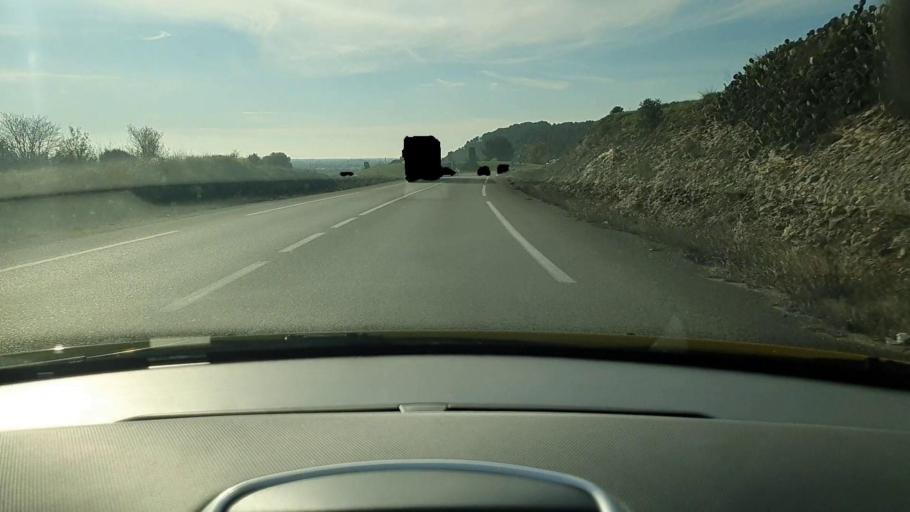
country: FR
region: Languedoc-Roussillon
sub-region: Departement du Gard
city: Comps
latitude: 43.8200
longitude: 4.6123
